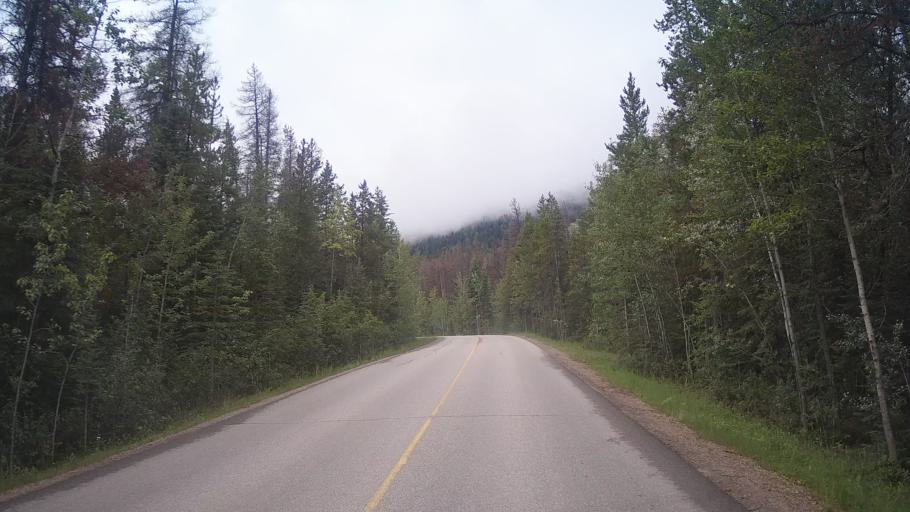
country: CA
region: Alberta
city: Jasper Park Lodge
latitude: 52.8557
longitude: -118.1032
